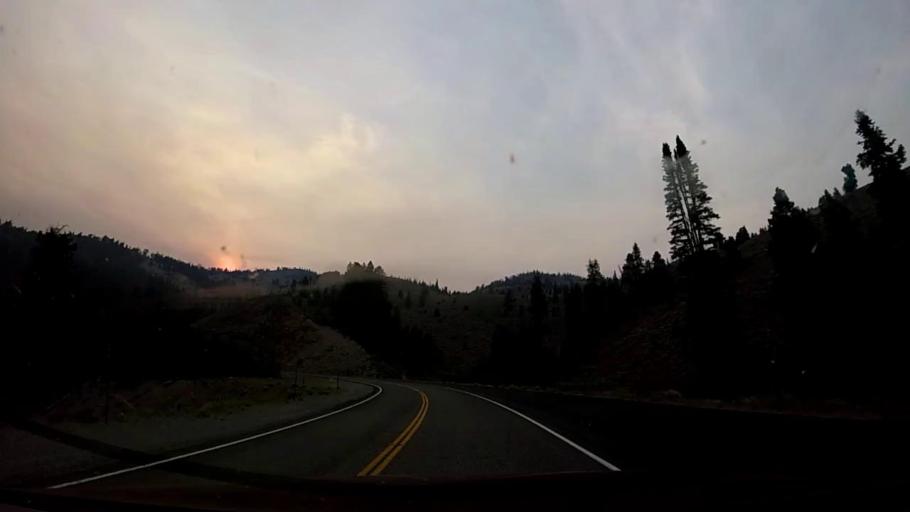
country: US
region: Idaho
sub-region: Blaine County
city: Ketchum
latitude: 43.8867
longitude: -114.6942
